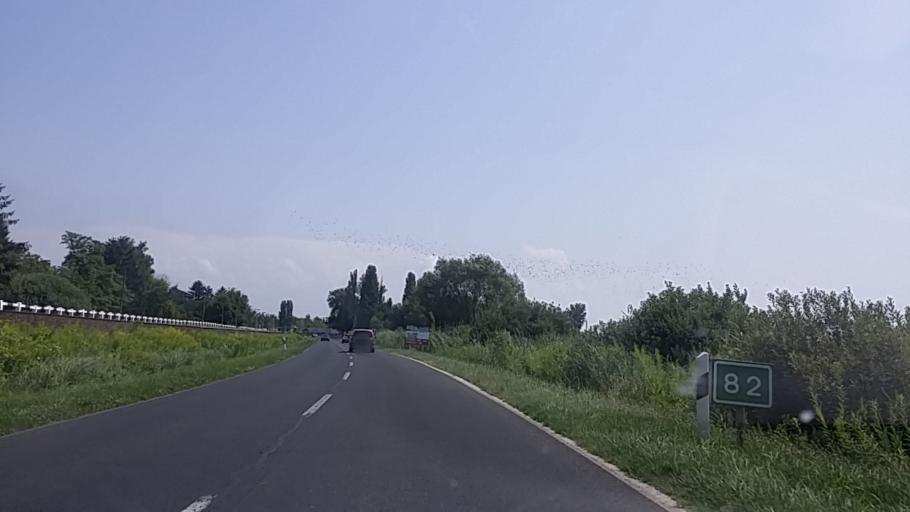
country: HU
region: Veszprem
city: Badacsonytomaj
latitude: 46.7933
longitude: 17.4708
